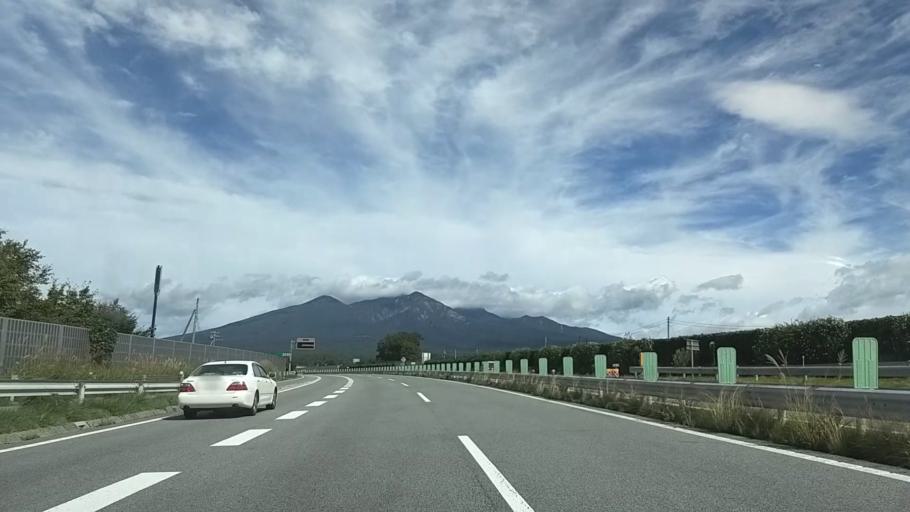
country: JP
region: Yamanashi
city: Nirasaki
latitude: 35.8312
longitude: 138.3925
